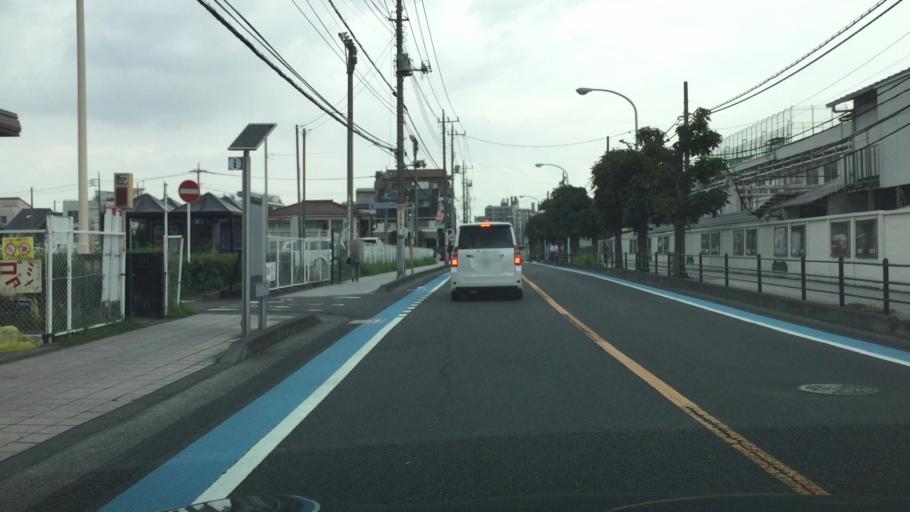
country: JP
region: Saitama
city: Yono
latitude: 35.9099
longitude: 139.6202
